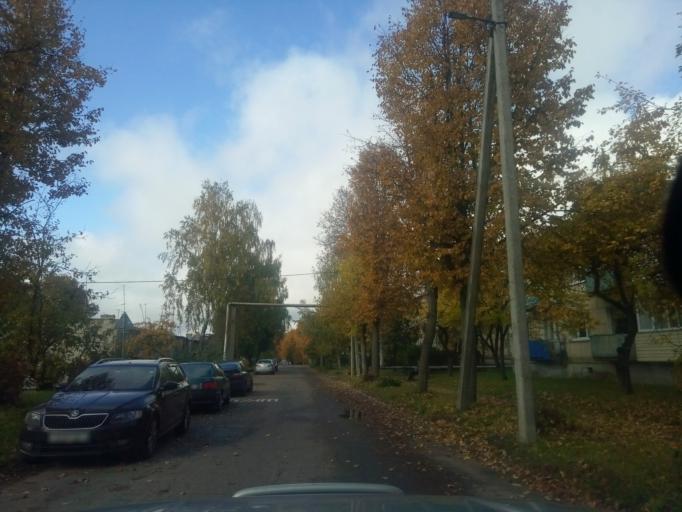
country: BY
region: Minsk
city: Zaslawye
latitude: 54.0103
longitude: 27.3047
